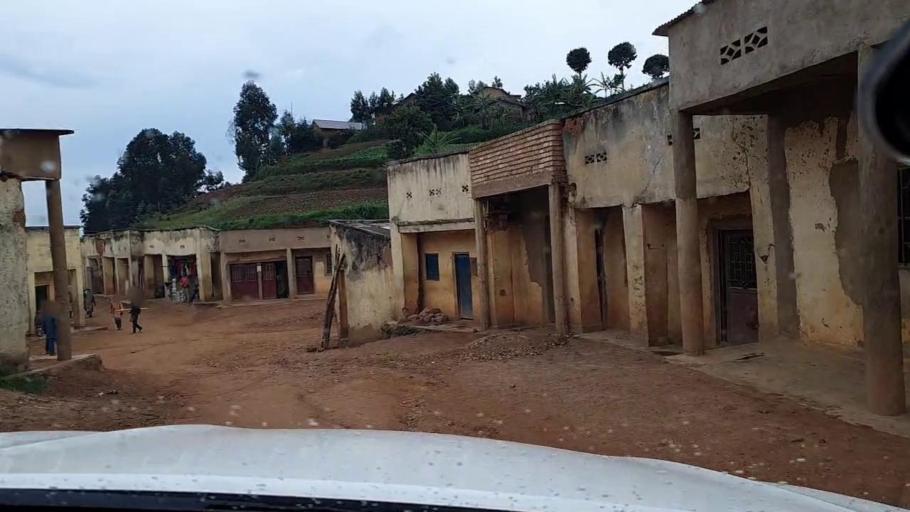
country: RW
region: Southern Province
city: Nzega
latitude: -2.3811
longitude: 29.2387
